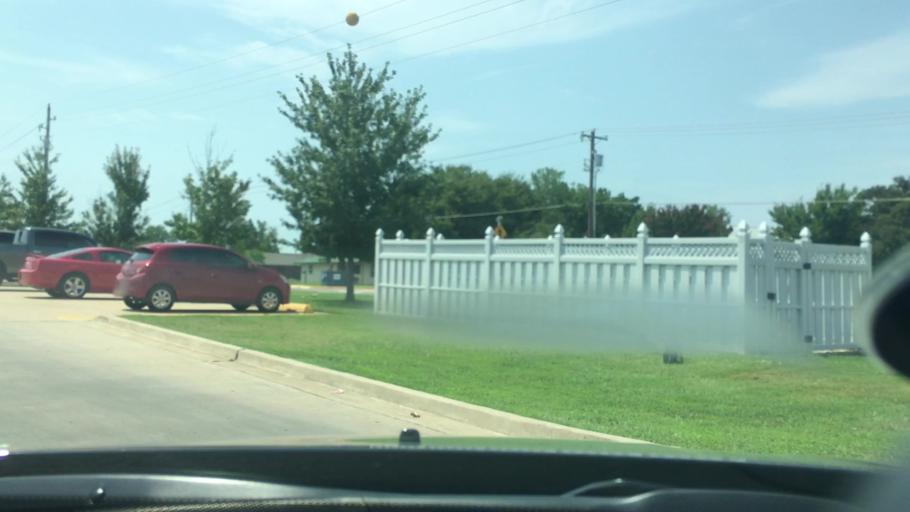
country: US
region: Oklahoma
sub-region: Pontotoc County
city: Ada
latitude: 34.7789
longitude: -96.6345
